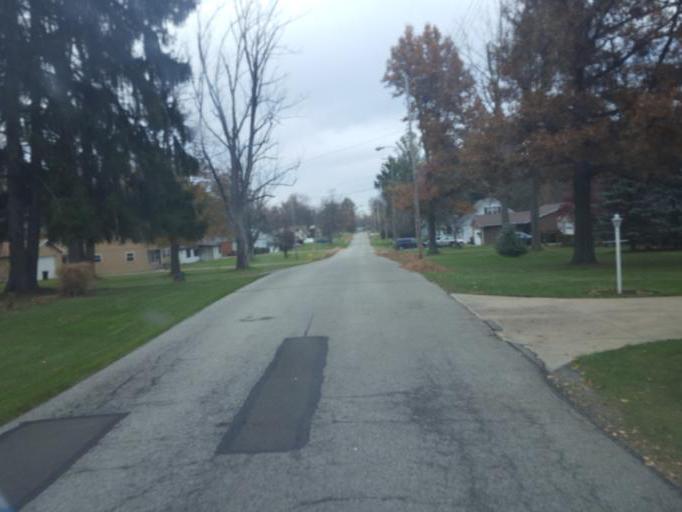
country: US
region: Ohio
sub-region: Richland County
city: Ontario
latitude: 40.7553
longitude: -82.5760
